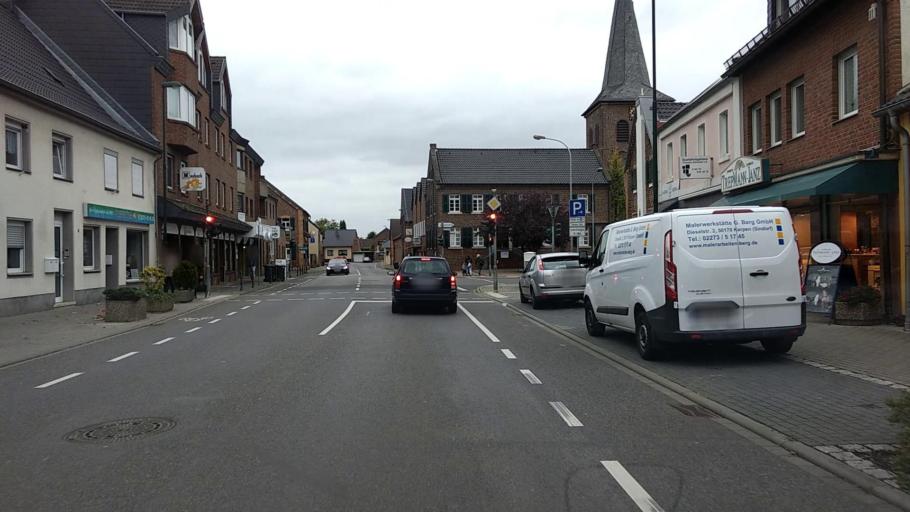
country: DE
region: North Rhine-Westphalia
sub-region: Regierungsbezirk Koln
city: Kerpen
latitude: 50.9080
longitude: 6.6728
